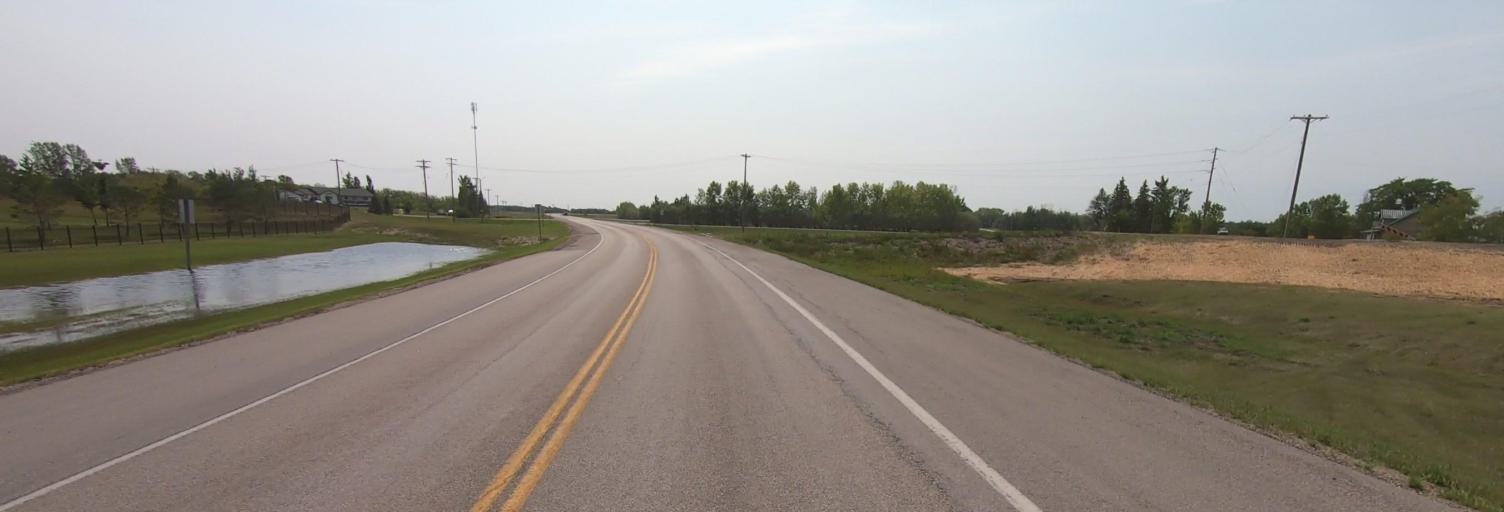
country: CA
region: Manitoba
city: Niverville
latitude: 49.6657
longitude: -97.1103
